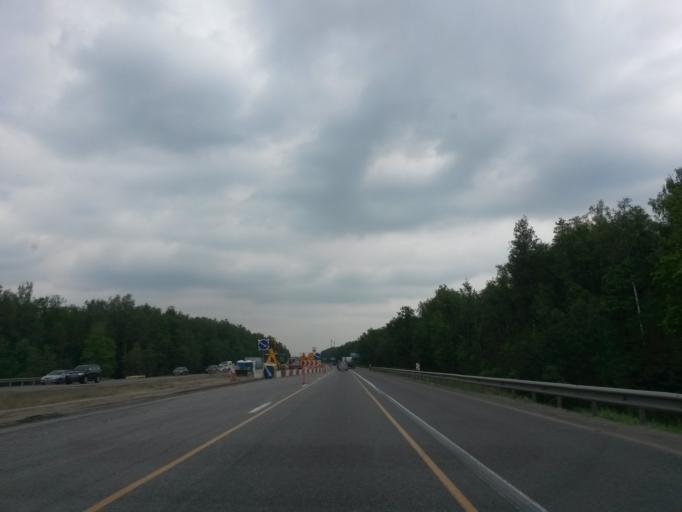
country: RU
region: Moskovskaya
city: Lyubuchany
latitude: 55.2143
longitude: 37.5348
